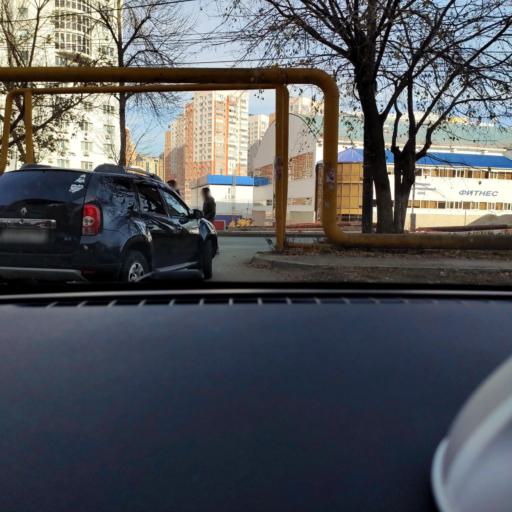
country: RU
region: Samara
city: Samara
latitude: 53.2389
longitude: 50.1796
